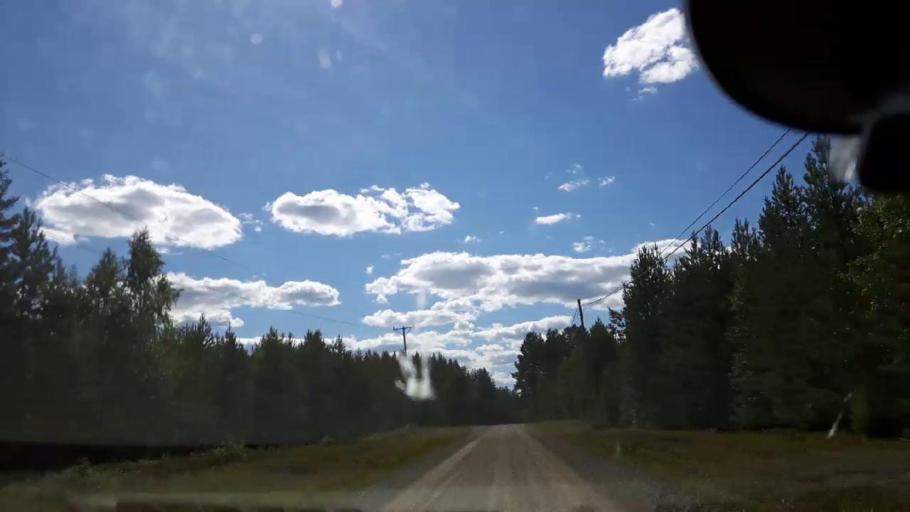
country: SE
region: Vaesternorrland
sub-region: Ange Kommun
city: Fransta
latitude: 62.7869
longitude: 16.0835
